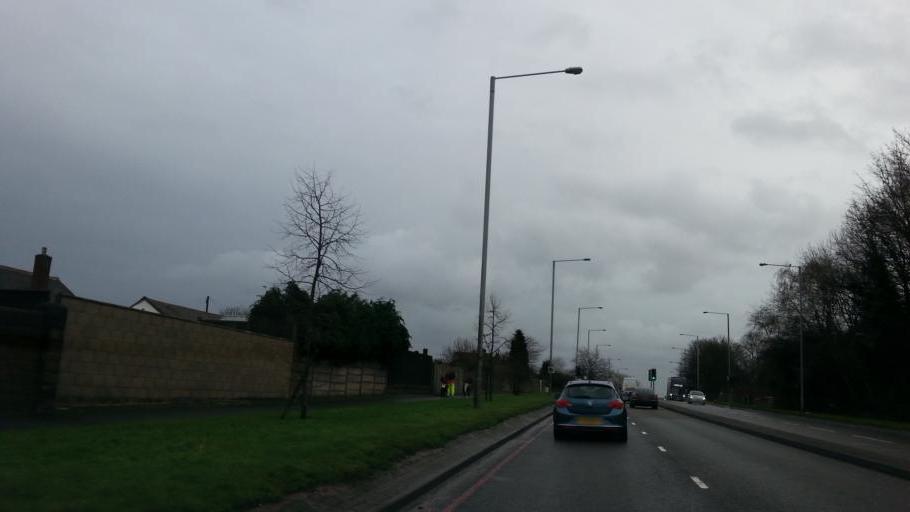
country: GB
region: England
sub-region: Sandwell
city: Oldbury
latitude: 52.5073
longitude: -2.0386
